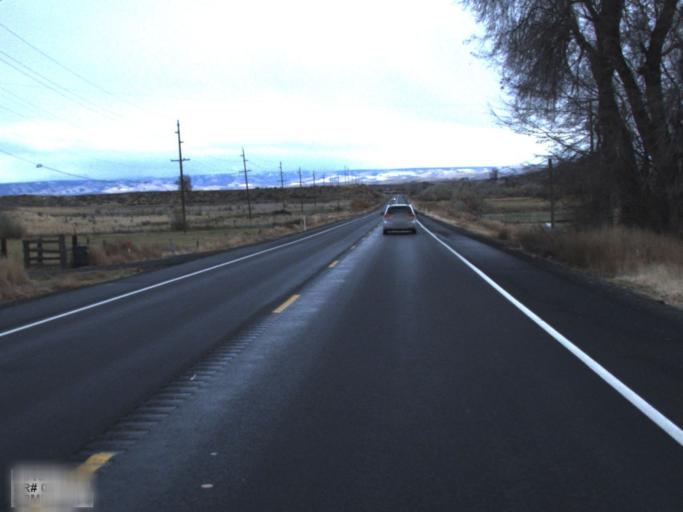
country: US
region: Washington
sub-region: Walla Walla County
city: Garrett
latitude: 46.0489
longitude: -118.7020
